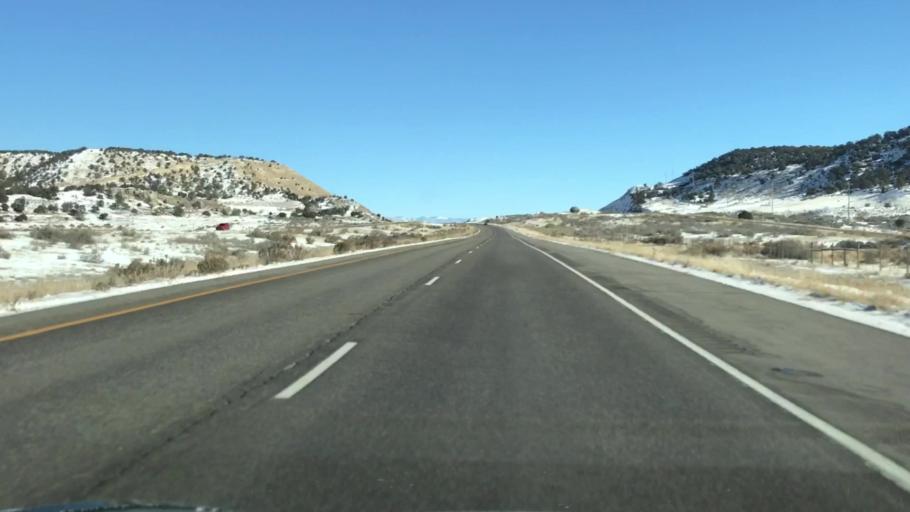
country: US
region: Colorado
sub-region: Garfield County
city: Rifle
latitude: 39.5053
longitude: -107.8902
